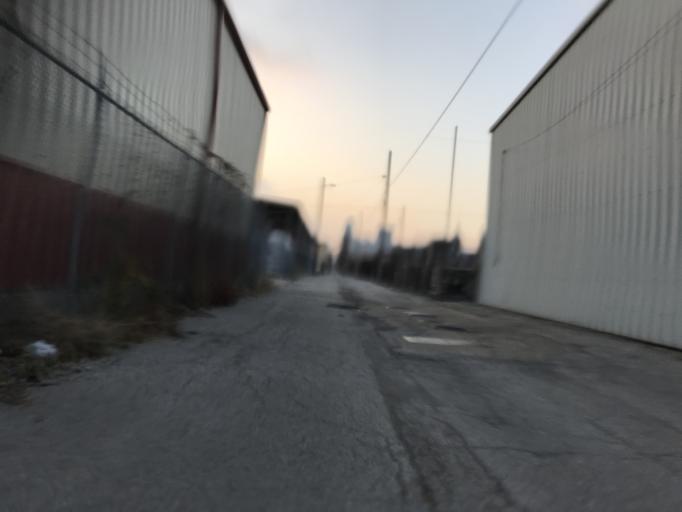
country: US
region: Kentucky
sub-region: Jefferson County
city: Louisville
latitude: 38.2522
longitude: -85.7350
